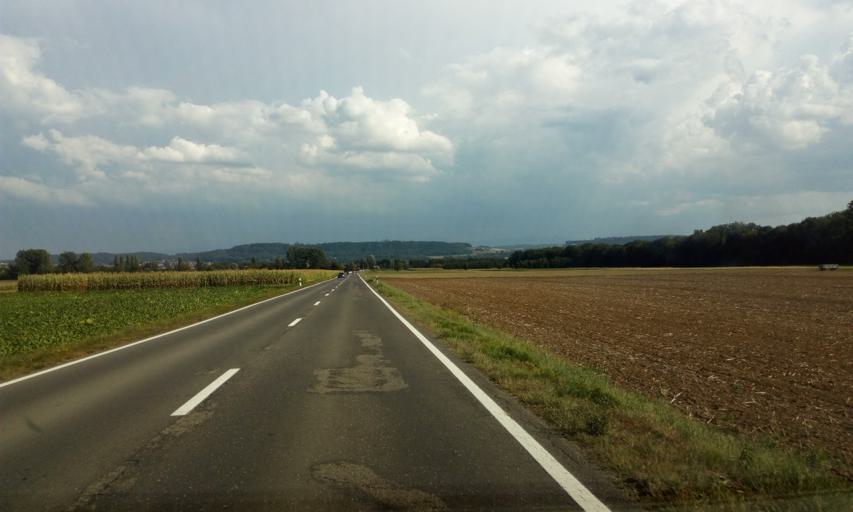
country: CH
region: Fribourg
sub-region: Broye District
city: Domdidier
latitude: 46.8971
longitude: 6.9976
